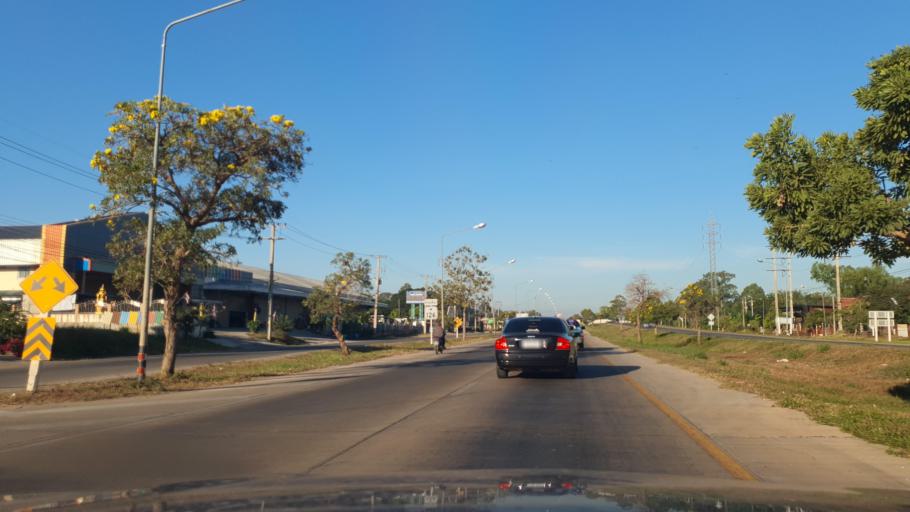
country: TH
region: Phitsanulok
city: Phitsanulok
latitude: 16.8648
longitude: 100.2479
